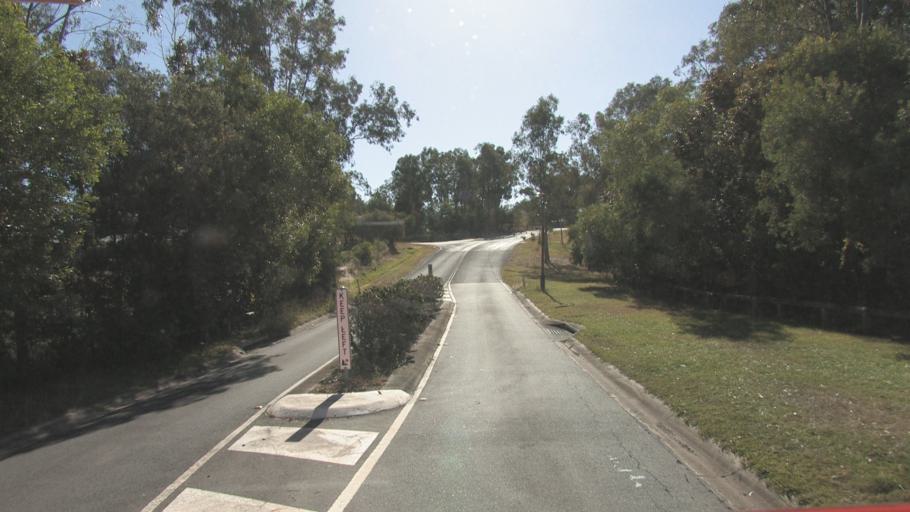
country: AU
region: Queensland
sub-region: Logan
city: Cedar Vale
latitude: -27.8616
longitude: 153.0376
